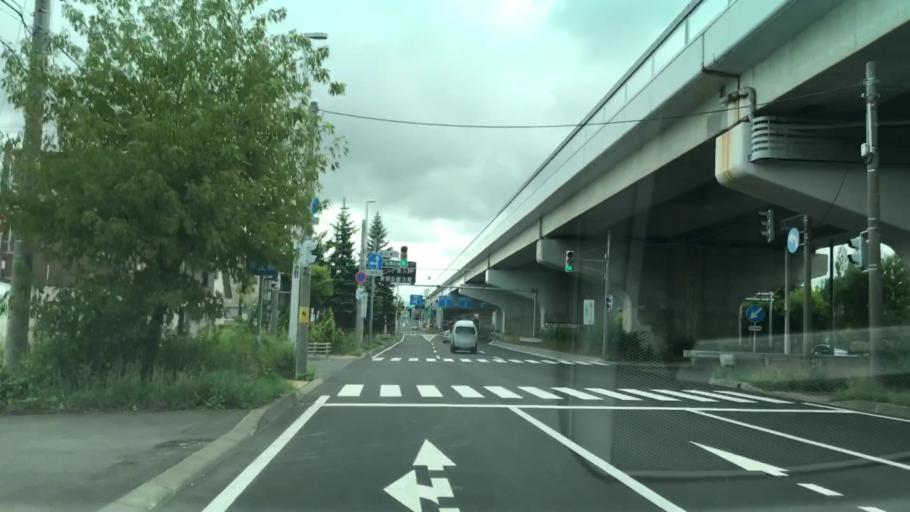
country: JP
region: Hokkaido
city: Sapporo
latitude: 43.1020
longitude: 141.3484
